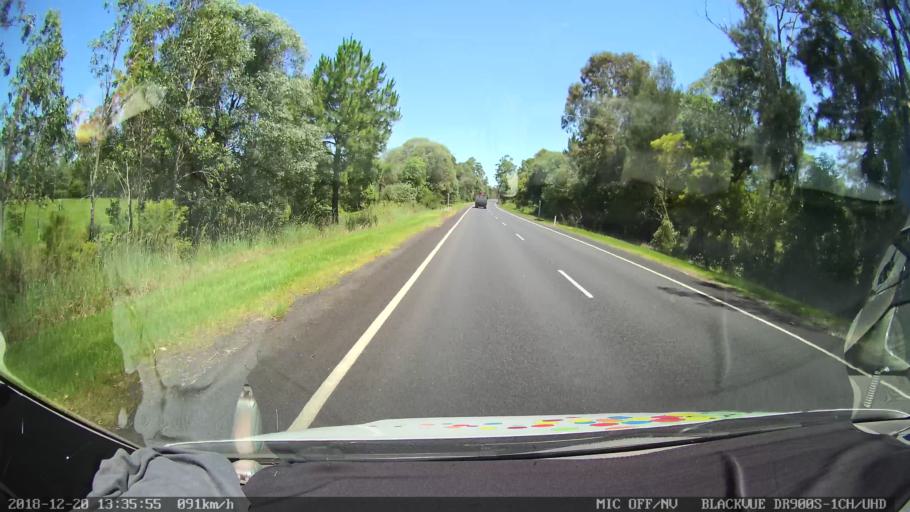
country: AU
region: New South Wales
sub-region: Clarence Valley
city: Maclean
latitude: -29.2758
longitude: 152.9914
